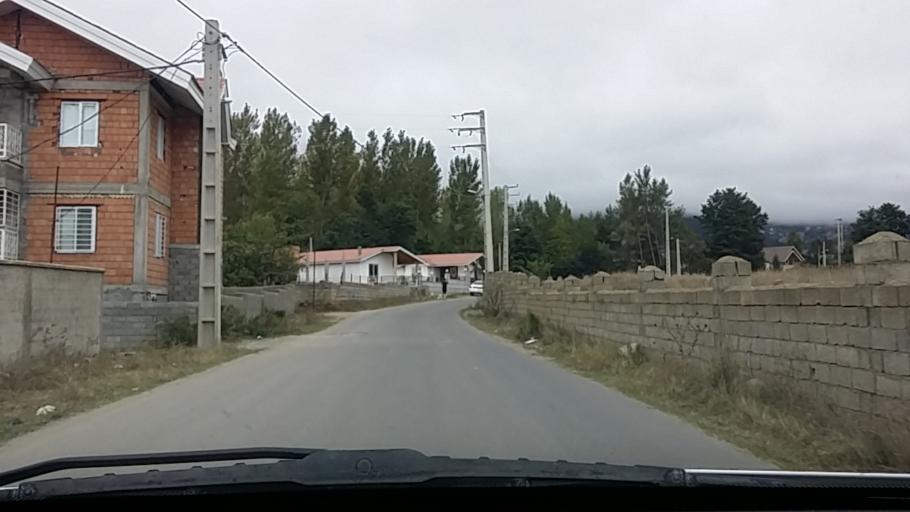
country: IR
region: Mazandaran
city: `Abbasabad
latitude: 36.5164
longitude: 51.1683
